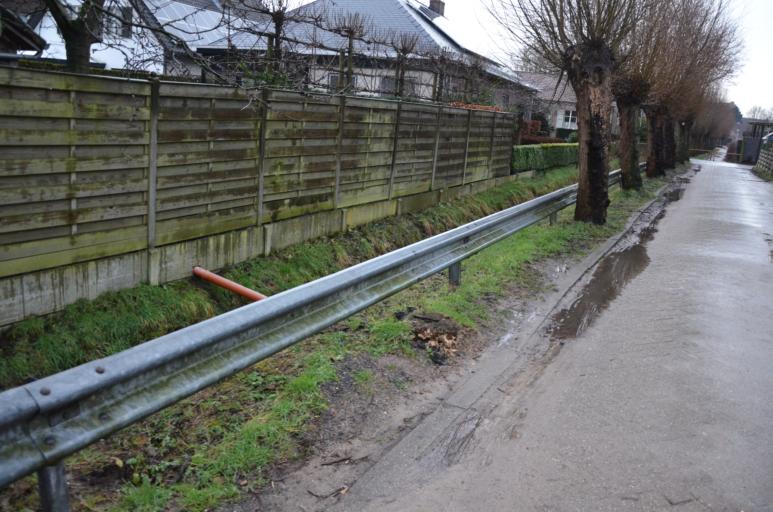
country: BE
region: Flanders
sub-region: Provincie Antwerpen
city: Zoersel
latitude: 51.3020
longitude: 4.6878
